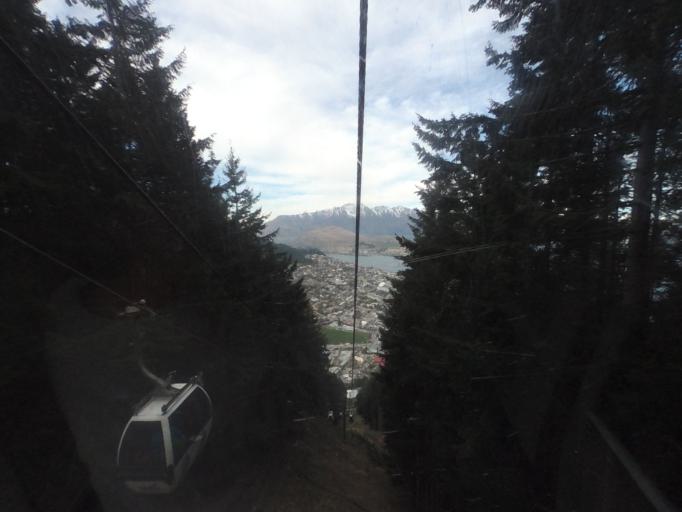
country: NZ
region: Otago
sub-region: Queenstown-Lakes District
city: Queenstown
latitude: -45.0272
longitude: 168.6511
